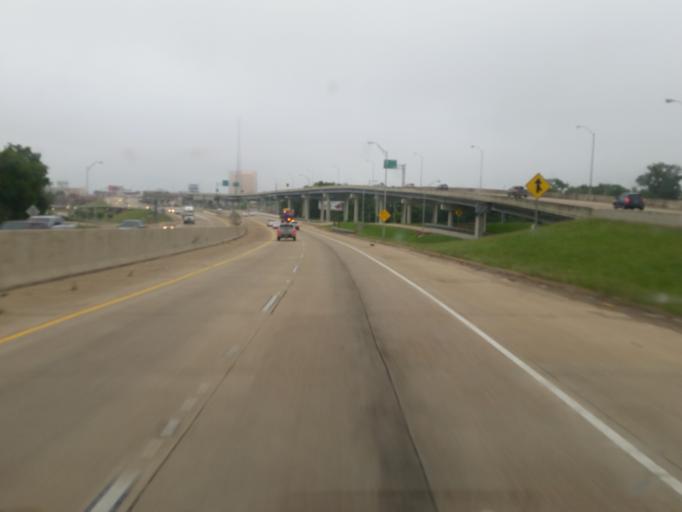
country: US
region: Louisiana
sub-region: Bossier Parish
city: Bossier City
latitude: 32.5026
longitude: -93.7485
